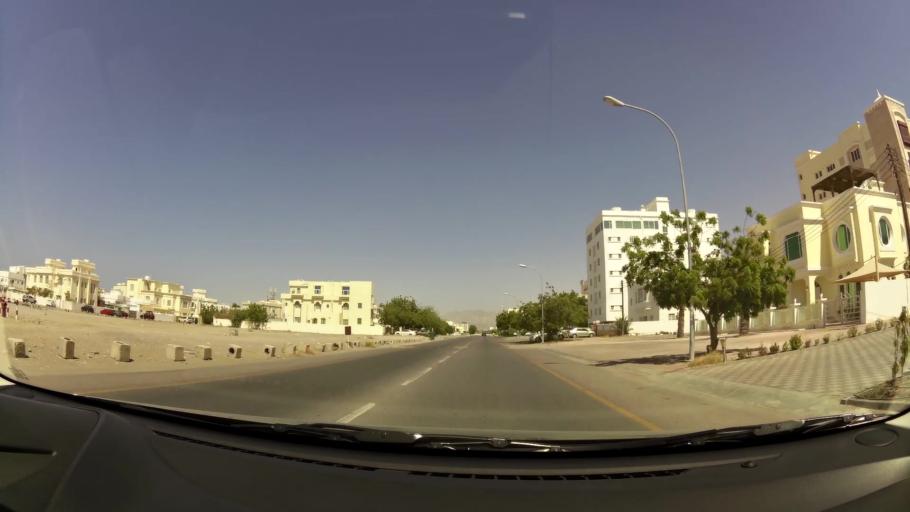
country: OM
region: Muhafazat Masqat
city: Bawshar
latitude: 23.5960
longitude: 58.3623
